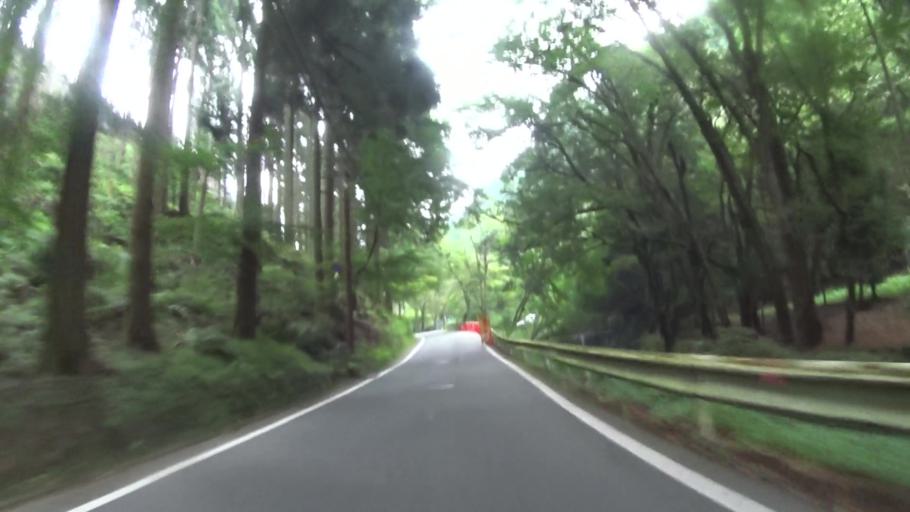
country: JP
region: Kyoto
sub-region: Kyoto-shi
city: Kamigyo-ku
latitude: 35.1148
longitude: 135.7603
